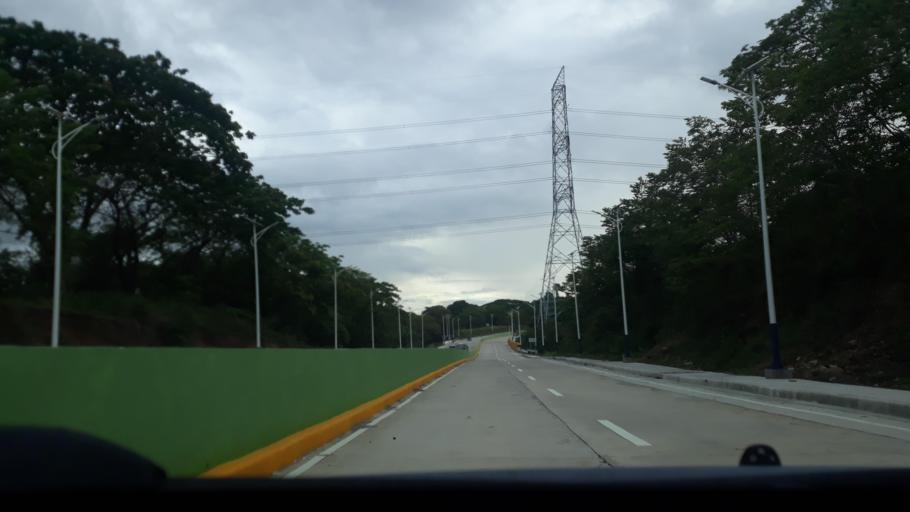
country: PH
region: Calabarzon
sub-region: Province of Cavite
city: Bulihan
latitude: 14.2919
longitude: 120.9698
